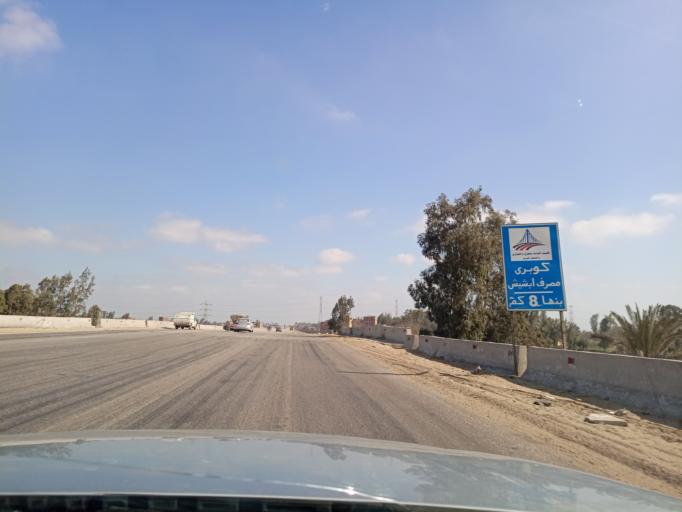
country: EG
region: Muhafazat al Minufiyah
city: Al Bajur
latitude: 30.4354
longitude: 31.1058
